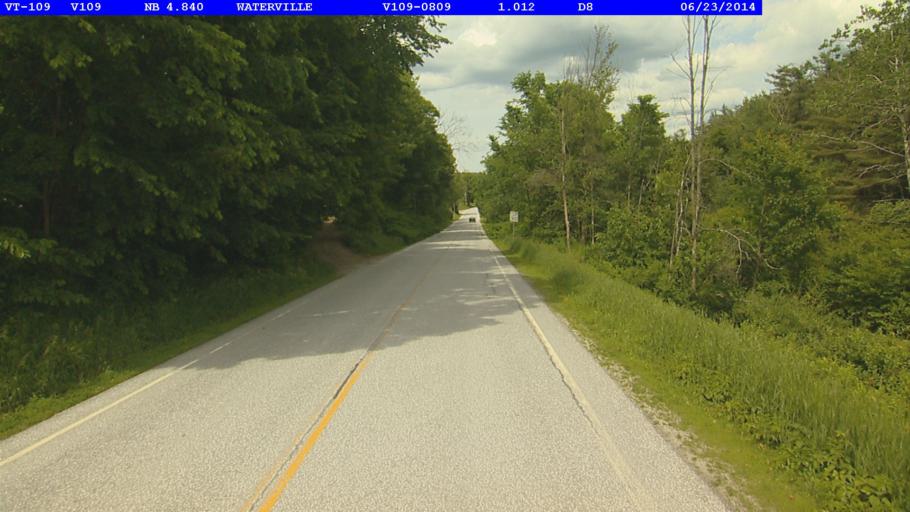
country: US
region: Vermont
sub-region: Lamoille County
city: Johnson
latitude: 44.6961
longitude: -72.7655
